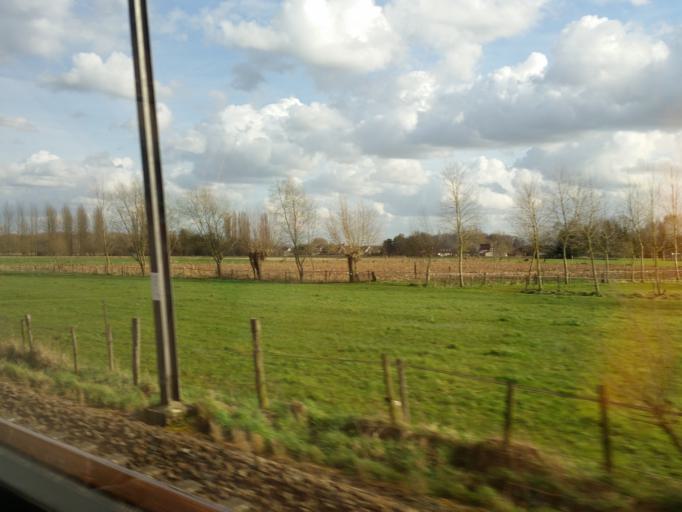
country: BE
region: Flanders
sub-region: Provincie Oost-Vlaanderen
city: Lebbeke
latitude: 51.0210
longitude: 4.1375
